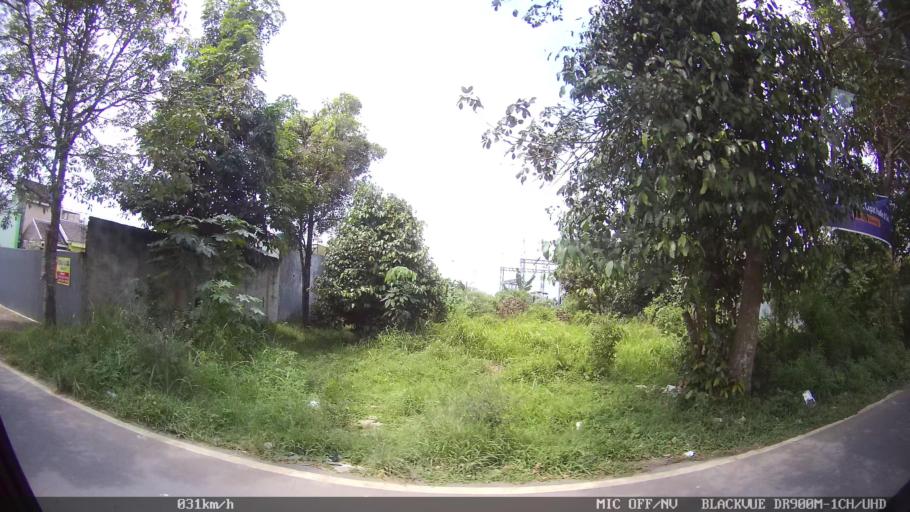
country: ID
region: Lampung
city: Kedaton
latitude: -5.3612
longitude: 105.3062
